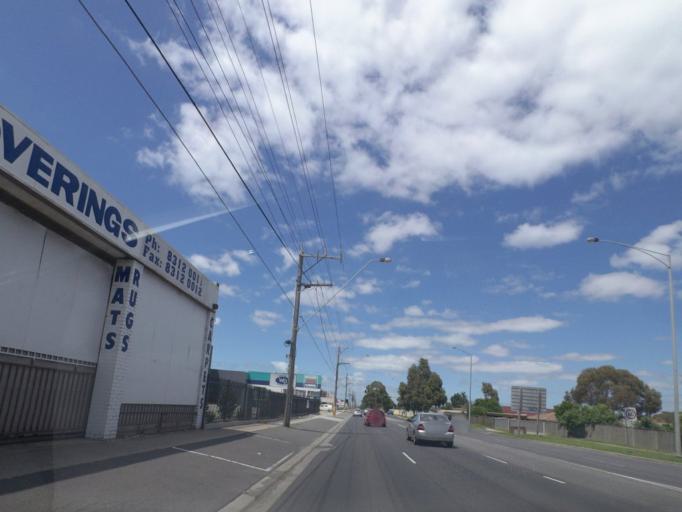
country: AU
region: Victoria
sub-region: Brimbank
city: Albion
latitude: -37.7534
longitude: 144.8331
